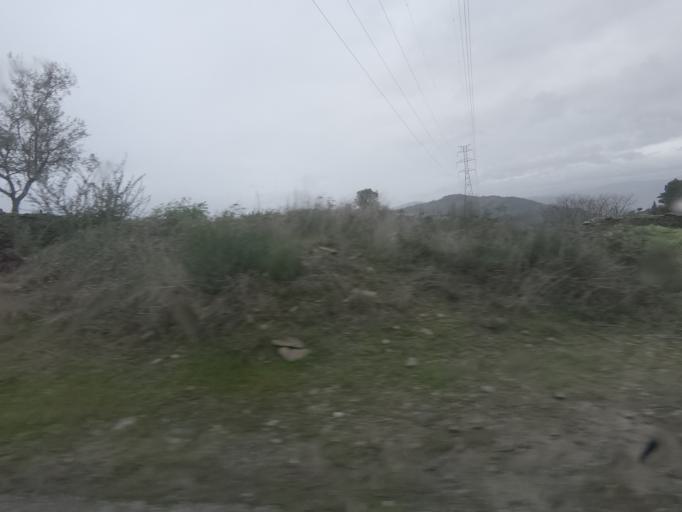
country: PT
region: Viseu
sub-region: Armamar
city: Armamar
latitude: 41.1618
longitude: -7.7111
